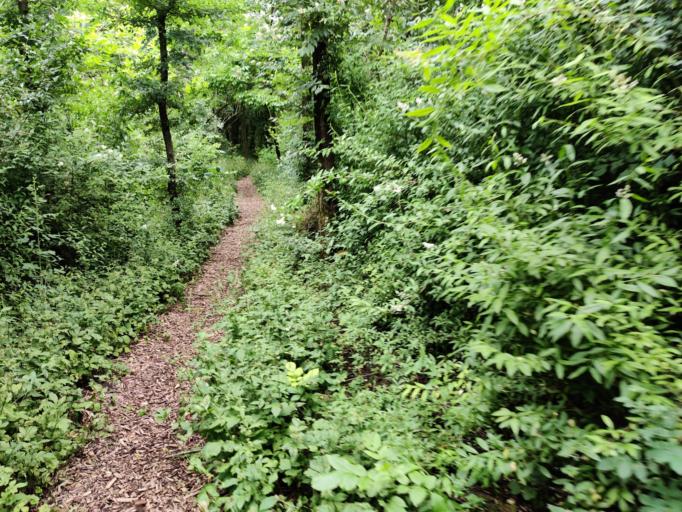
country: HU
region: Hajdu-Bihar
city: Balmazujvaros
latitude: 47.6129
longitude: 21.3282
